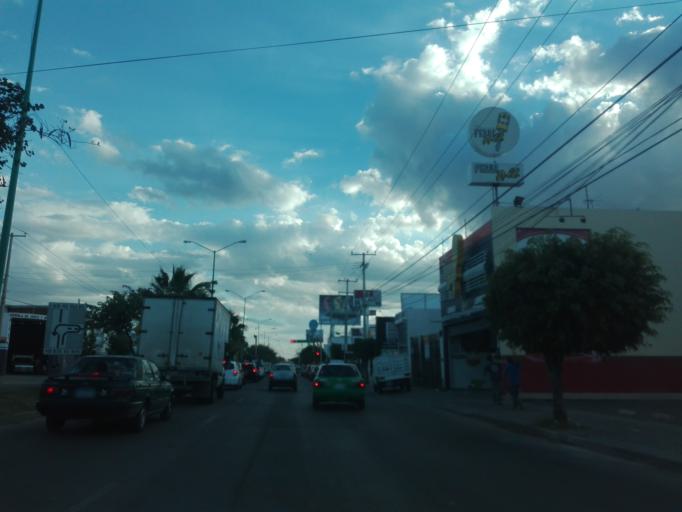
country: MX
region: Guanajuato
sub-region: Leon
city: San Jose de Duran (Los Troncoso)
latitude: 21.0924
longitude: -101.6644
